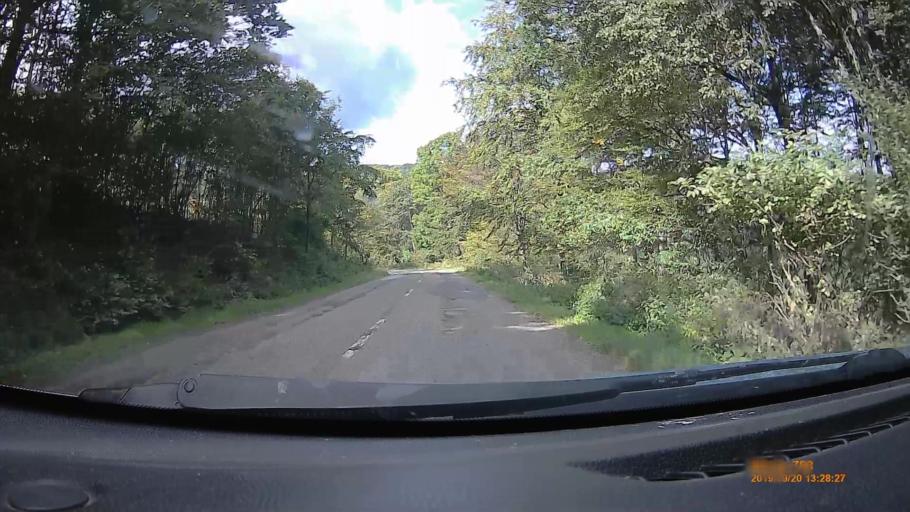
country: HU
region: Heves
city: Szilvasvarad
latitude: 48.0469
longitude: 20.4865
